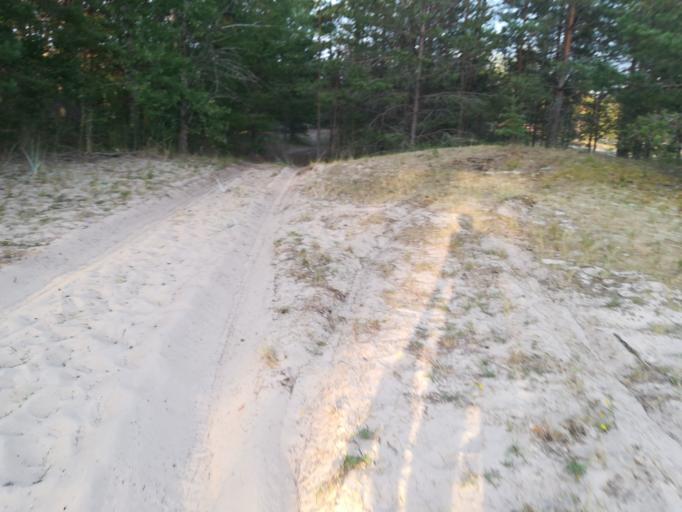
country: RU
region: Leningrad
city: Ust'-Luga
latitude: 59.6772
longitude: 28.2434
